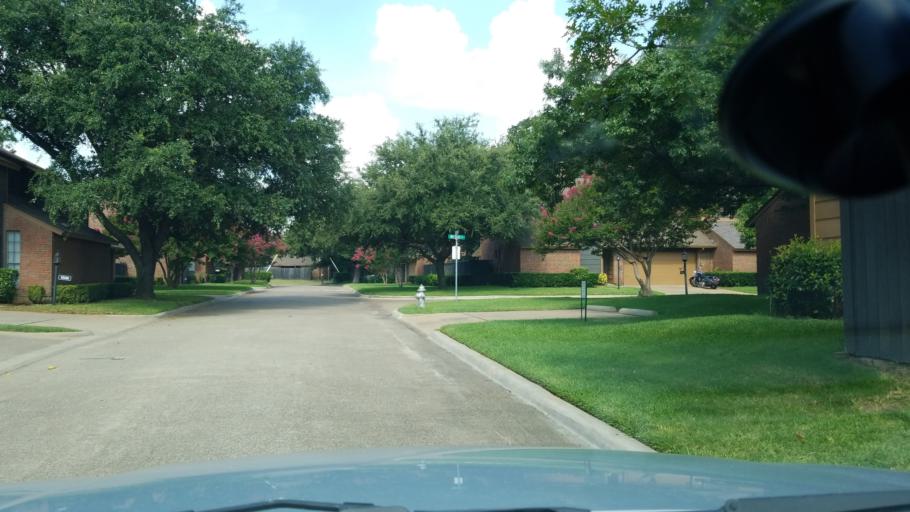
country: US
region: Texas
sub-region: Dallas County
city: Irving
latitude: 32.8334
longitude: -96.9266
